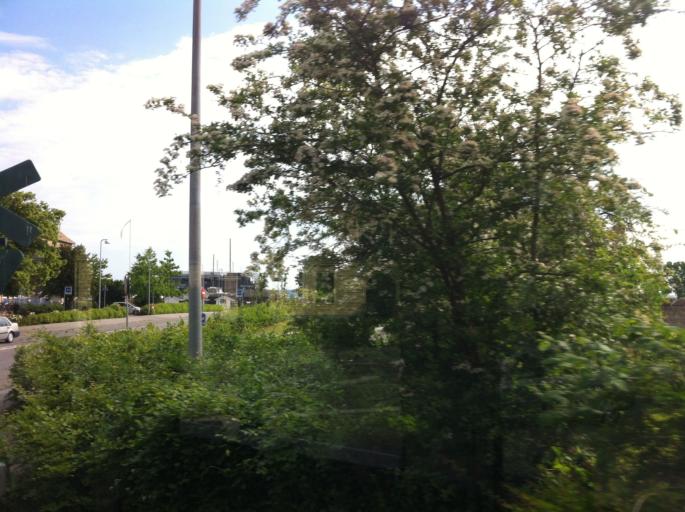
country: DK
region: Capital Region
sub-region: Helsingor Kommune
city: Helsingor
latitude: 56.0391
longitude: 12.6128
